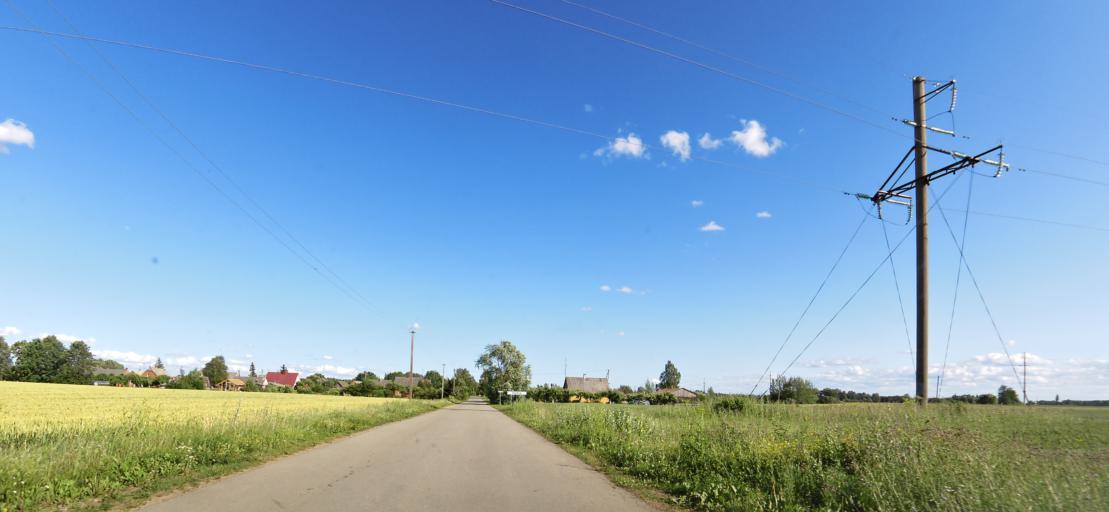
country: LT
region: Panevezys
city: Pasvalys
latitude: 56.1370
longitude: 24.5351
